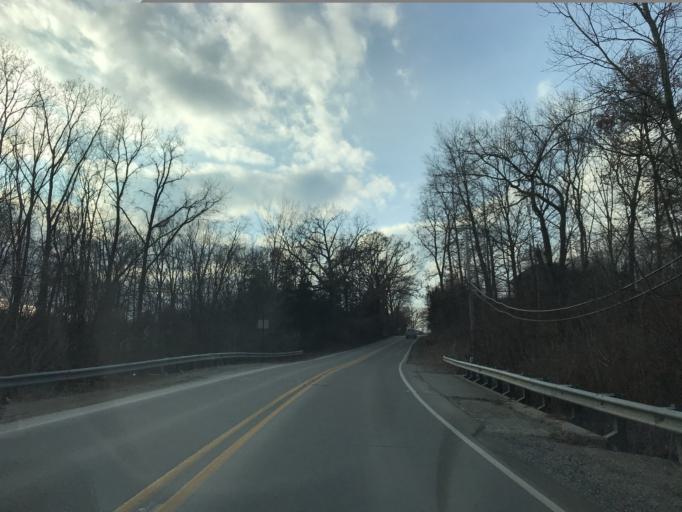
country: US
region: Michigan
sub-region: Livingston County
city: Whitmore Lake
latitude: 42.4662
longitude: -83.7065
